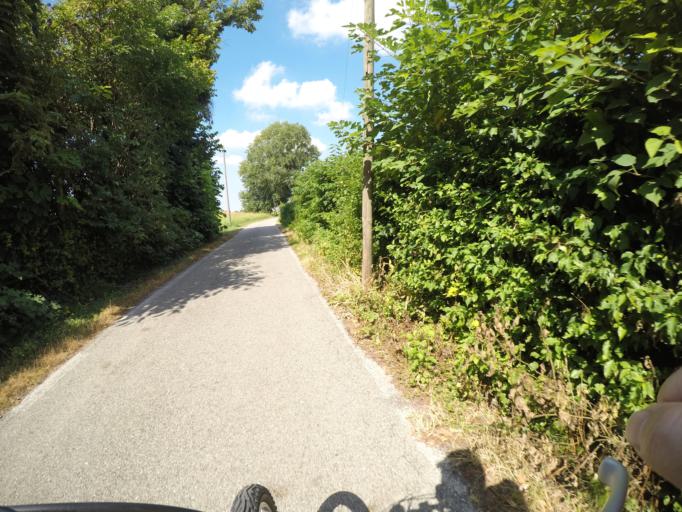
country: IT
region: Veneto
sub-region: Provincia di Rovigo
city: Lendinara
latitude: 45.0735
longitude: 11.6100
